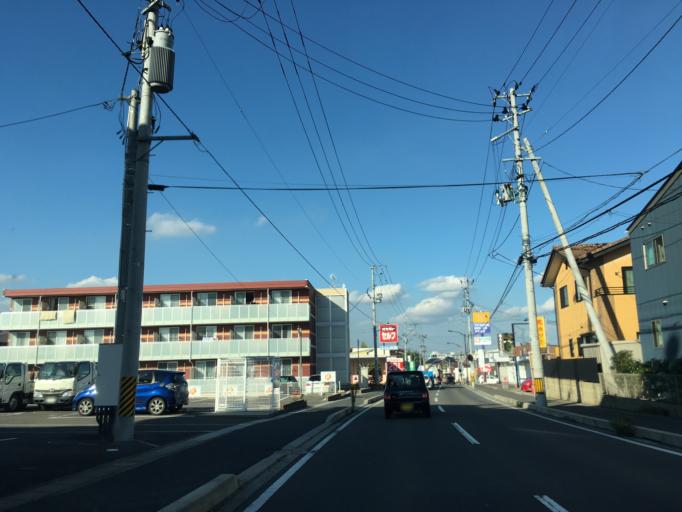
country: JP
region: Fukushima
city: Koriyama
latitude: 37.4015
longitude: 140.3344
